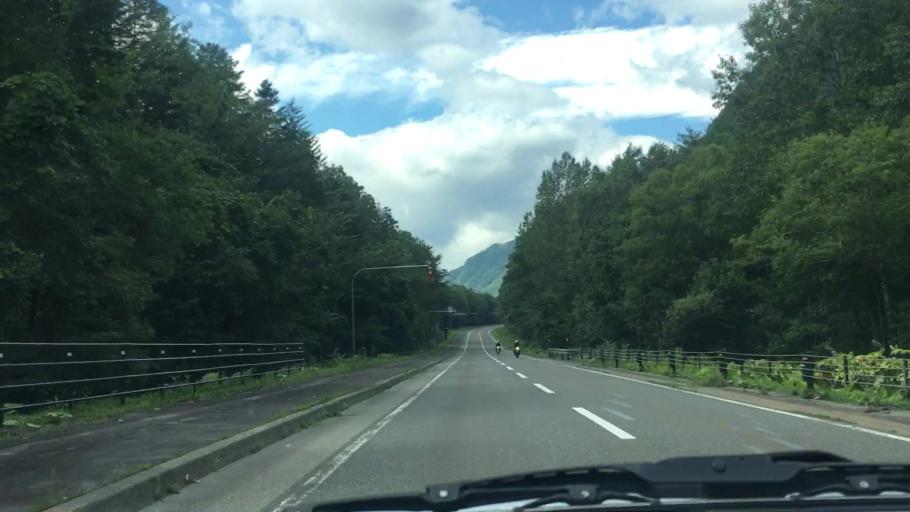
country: JP
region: Hokkaido
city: Otofuke
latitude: 43.3494
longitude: 143.2683
